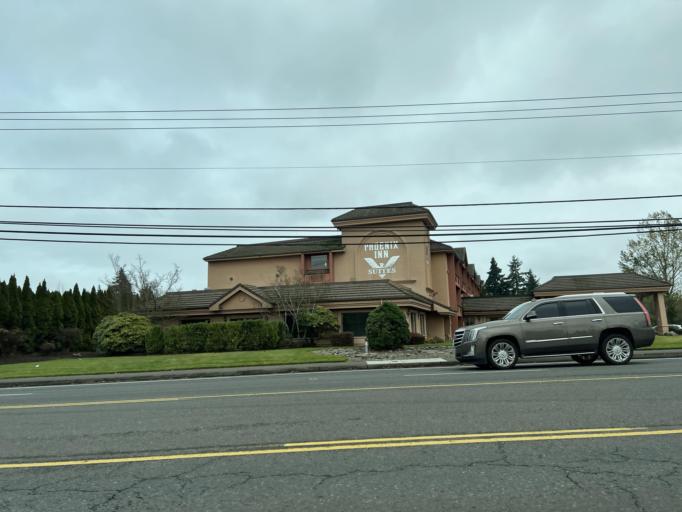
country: US
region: Oregon
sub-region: Marion County
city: Salem
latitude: 44.8914
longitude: -123.0352
